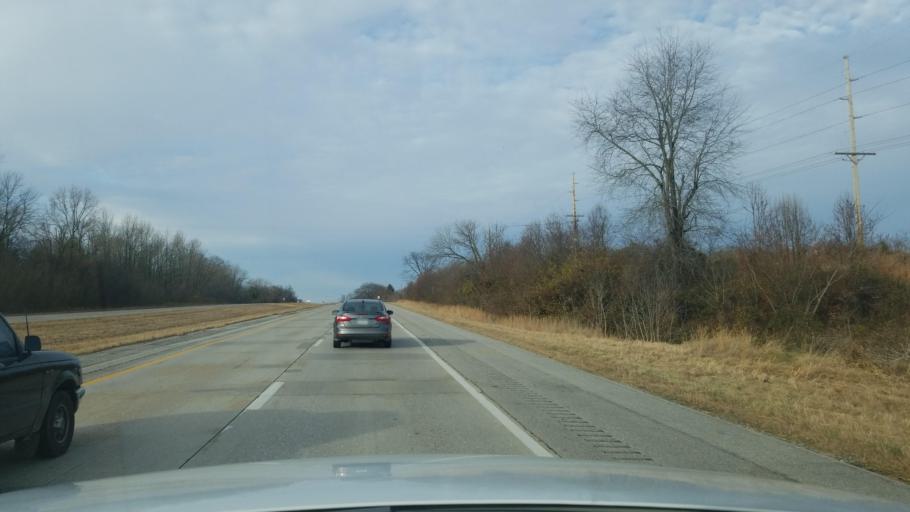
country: US
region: Indiana
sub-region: Posey County
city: Mount Vernon
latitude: 37.9426
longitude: -87.7259
